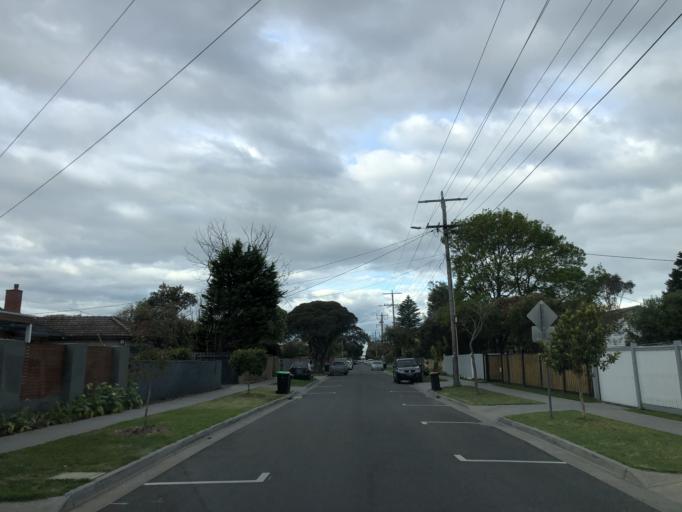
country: AU
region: Victoria
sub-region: Kingston
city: Bonbeach
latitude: -38.0614
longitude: 145.1272
